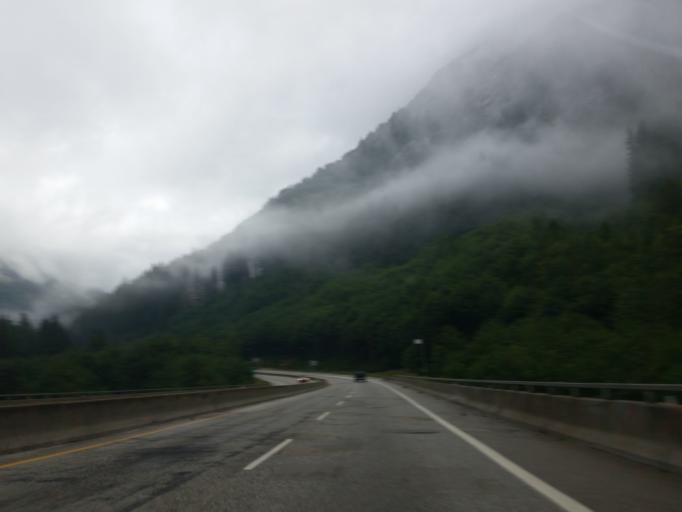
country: CA
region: British Columbia
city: Hope
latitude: 49.5057
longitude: -121.1994
